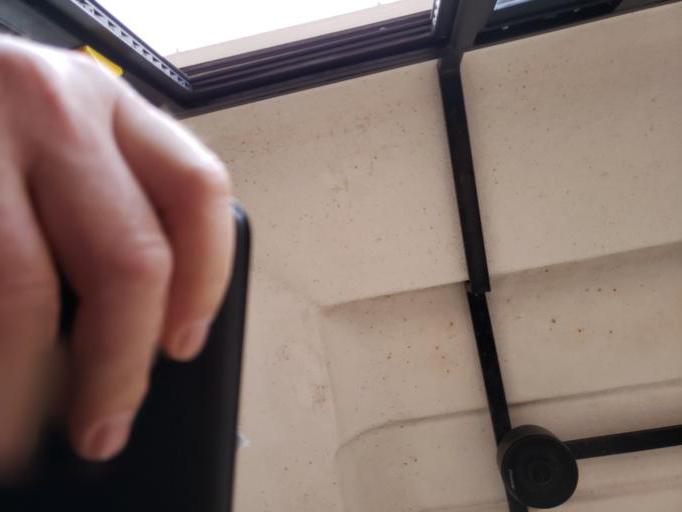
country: RU
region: Moscow
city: Kolomenskoye
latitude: 55.6740
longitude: 37.6703
